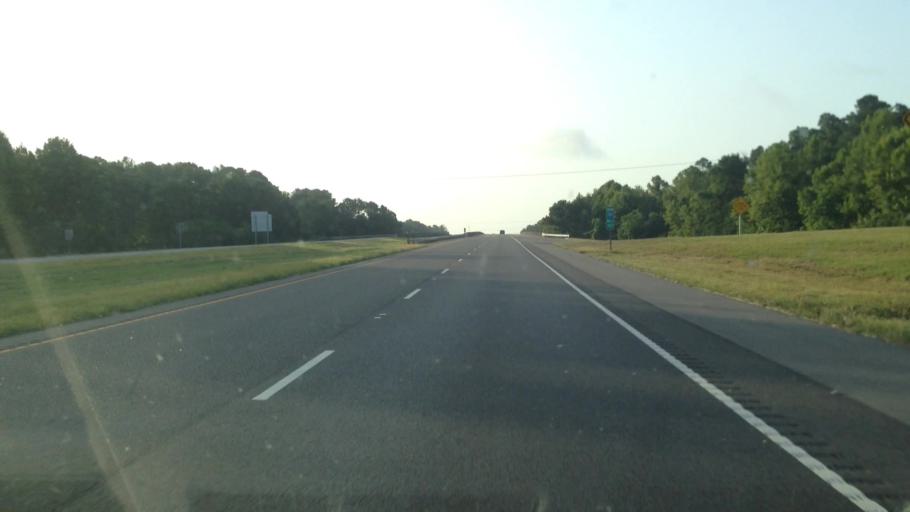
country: US
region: Louisiana
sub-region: Rapides Parish
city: Boyce
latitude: 31.4083
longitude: -92.7154
